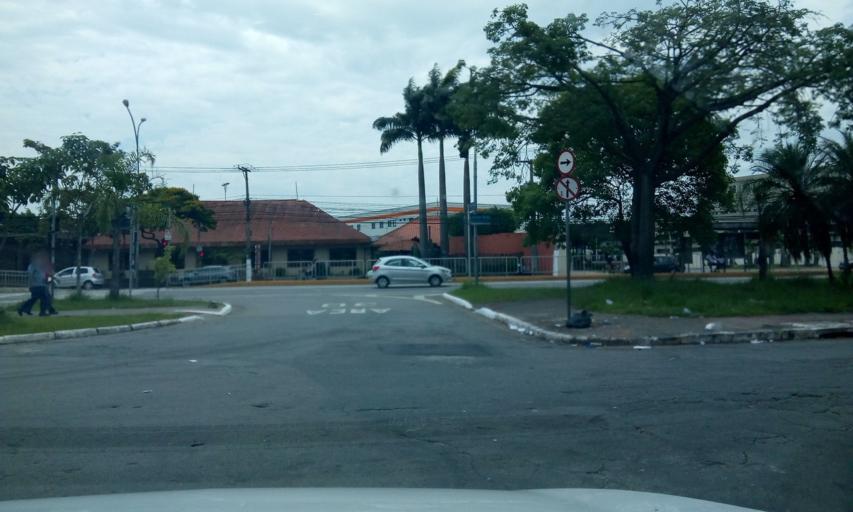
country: BR
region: Sao Paulo
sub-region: Sao Paulo
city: Sao Paulo
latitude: -23.5143
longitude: -46.7027
